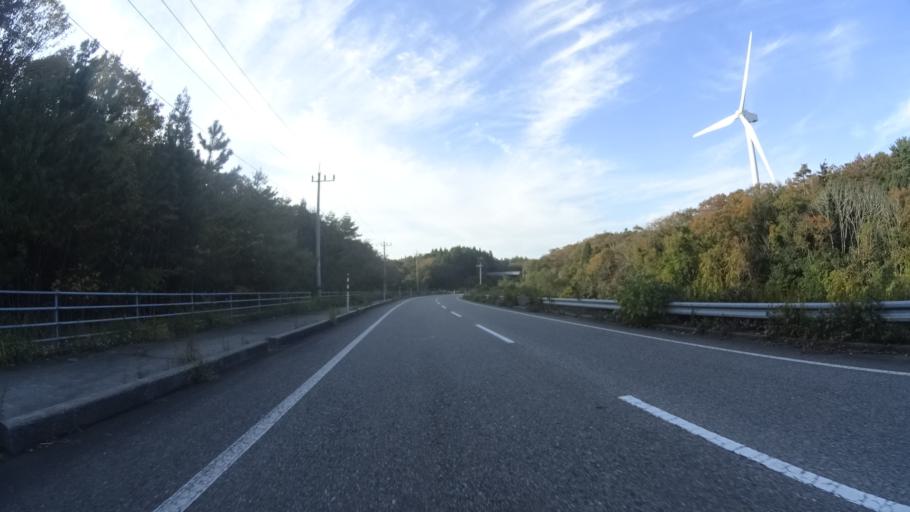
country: JP
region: Ishikawa
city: Hakui
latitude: 37.0739
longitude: 136.7320
